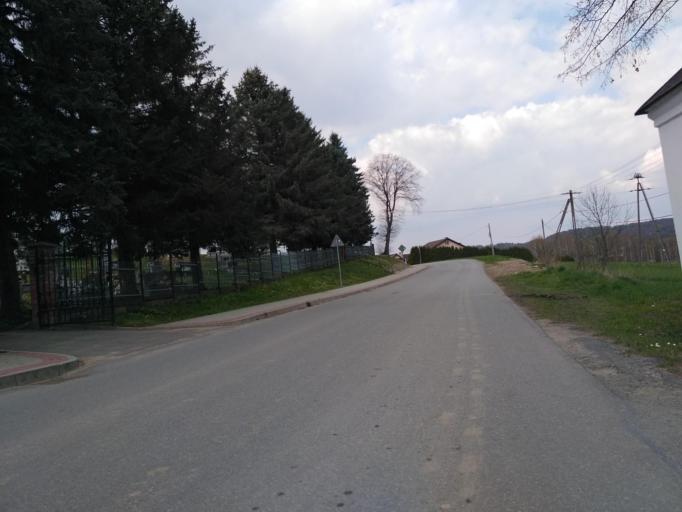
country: PL
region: Subcarpathian Voivodeship
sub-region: Powiat sanocki
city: Strachocina
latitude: 49.6033
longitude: 22.0924
